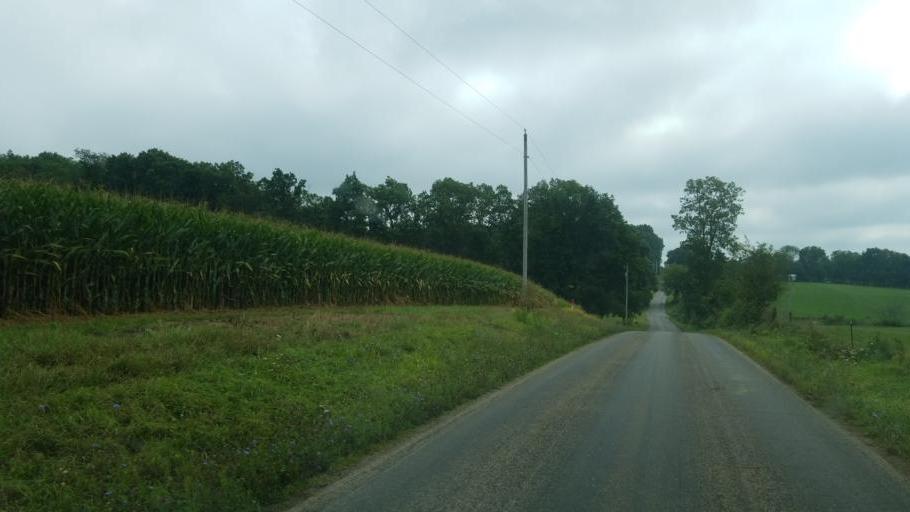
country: US
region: Ohio
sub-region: Licking County
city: Utica
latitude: 40.2562
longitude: -82.3765
